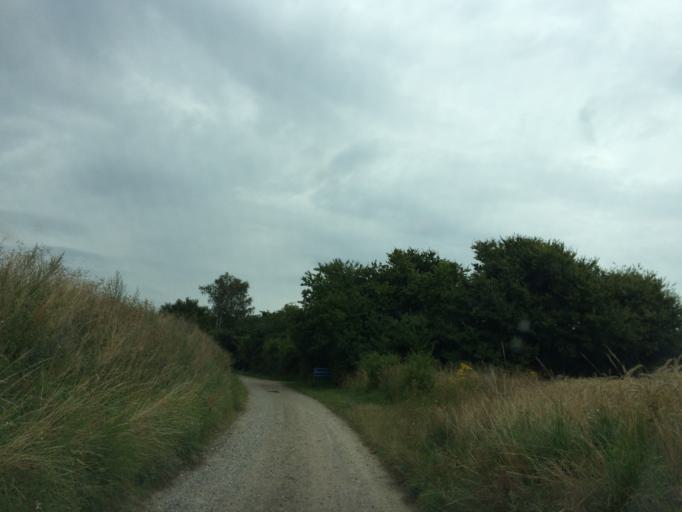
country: DK
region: Central Jutland
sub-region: Syddjurs Kommune
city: Ronde
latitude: 56.2394
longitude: 10.5542
